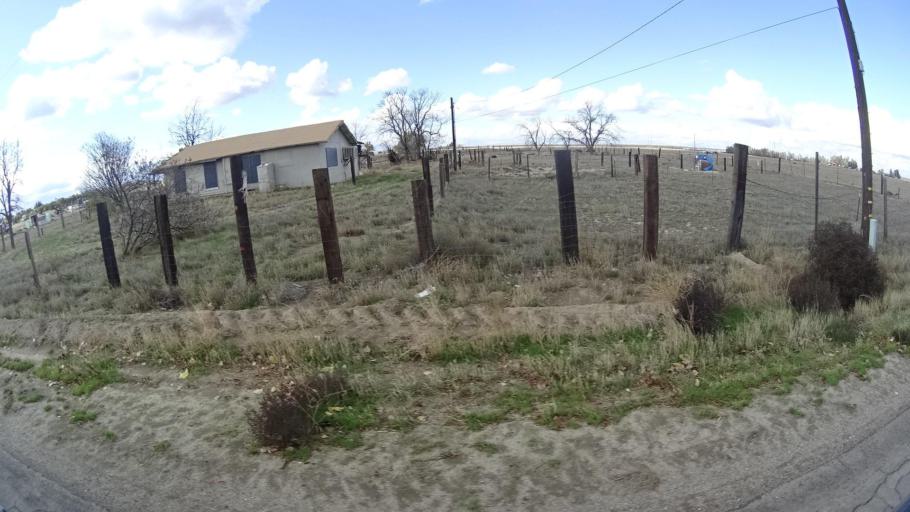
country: US
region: California
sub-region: Kern County
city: Greenfield
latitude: 35.2309
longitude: -119.0931
